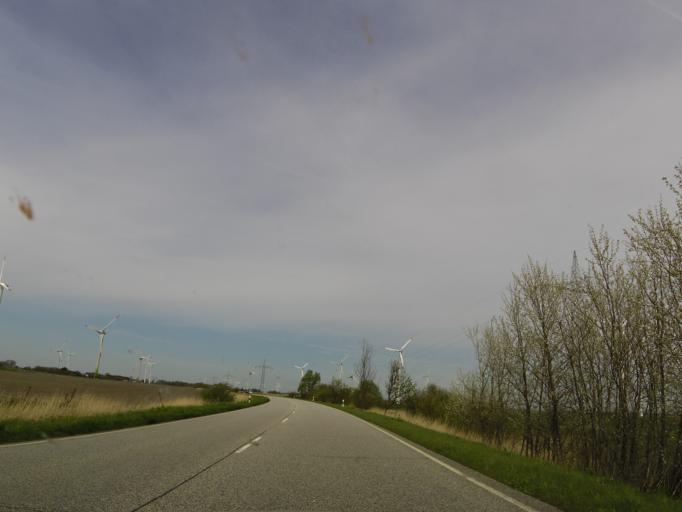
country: DE
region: Schleswig-Holstein
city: Stelle-Wittenwurth
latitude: 54.2613
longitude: 9.0342
